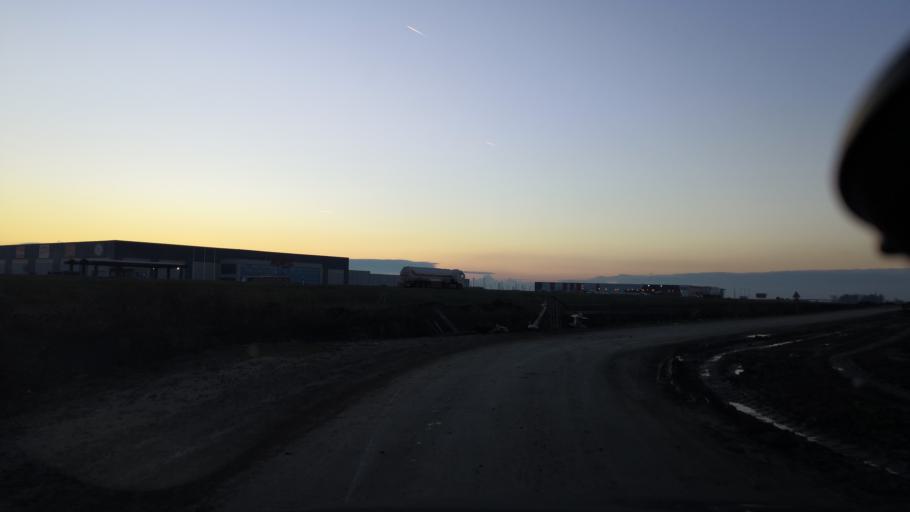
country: RS
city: Simanovci
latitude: 44.8887
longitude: 20.0982
